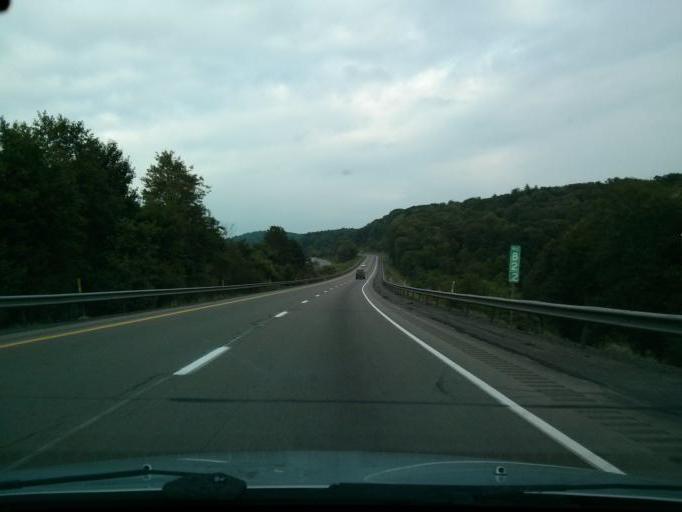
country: US
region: Pennsylvania
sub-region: Jefferson County
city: Brookville
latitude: 41.1695
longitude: -79.0311
